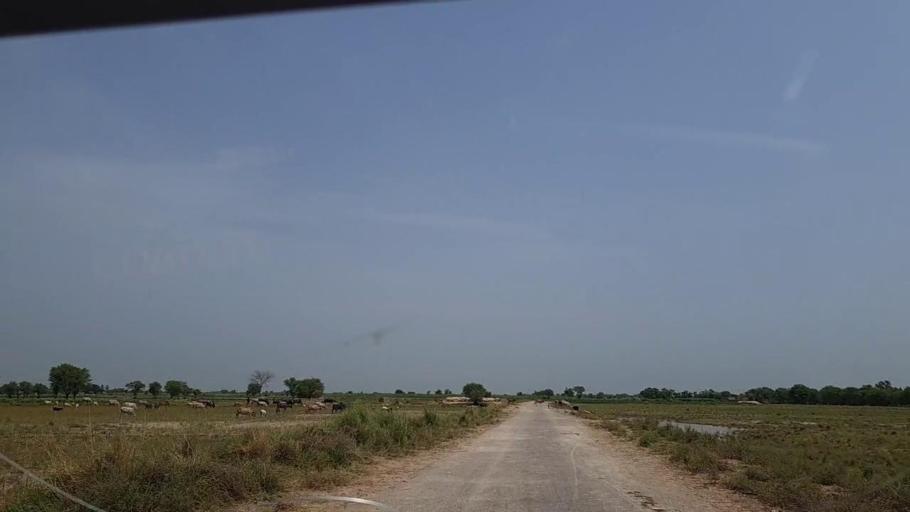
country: PK
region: Sindh
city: Tharu Shah
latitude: 26.9027
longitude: 68.0538
